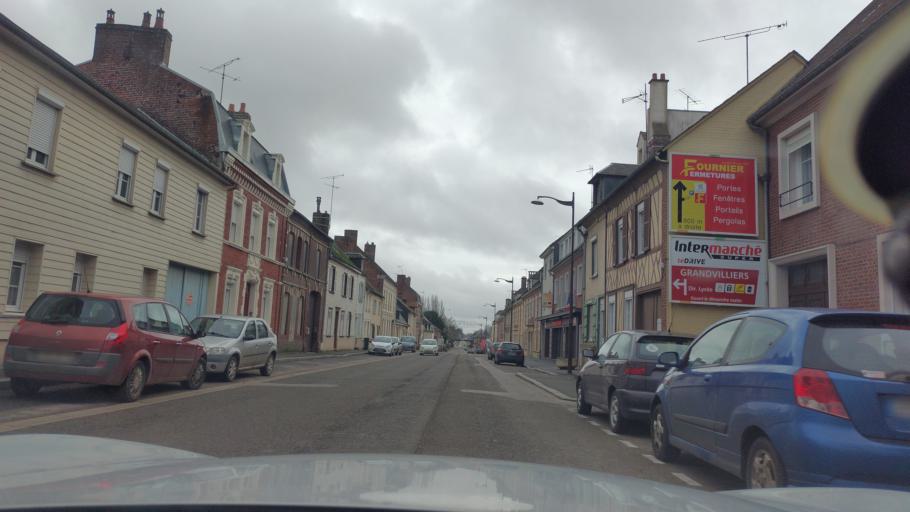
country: FR
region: Picardie
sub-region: Departement de l'Oise
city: Grandvilliers
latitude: 49.6633
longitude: 1.9403
